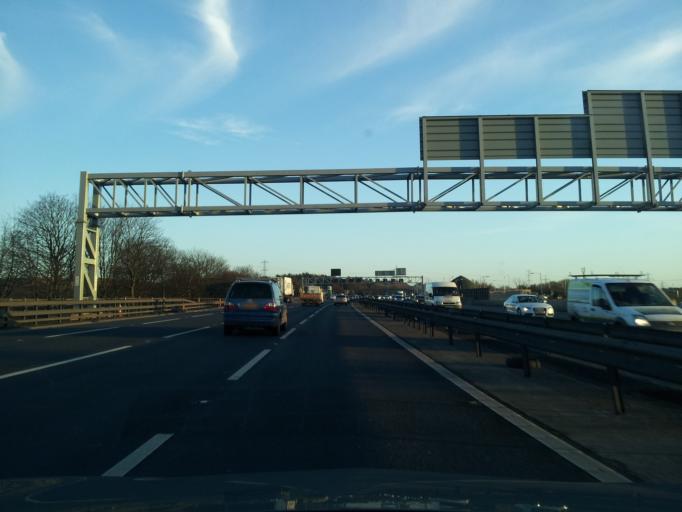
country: GB
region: England
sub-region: Central Bedfordshire
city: Harlington
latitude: 51.9511
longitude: -0.5061
